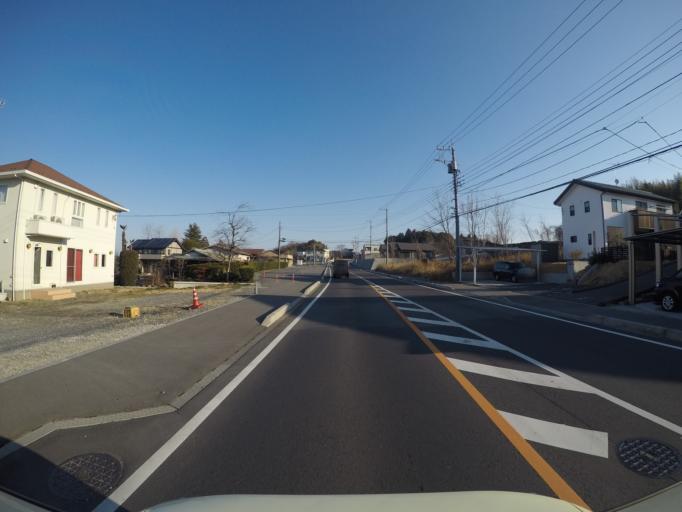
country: JP
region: Tochigi
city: Utsunomiya-shi
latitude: 36.5399
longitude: 139.9664
